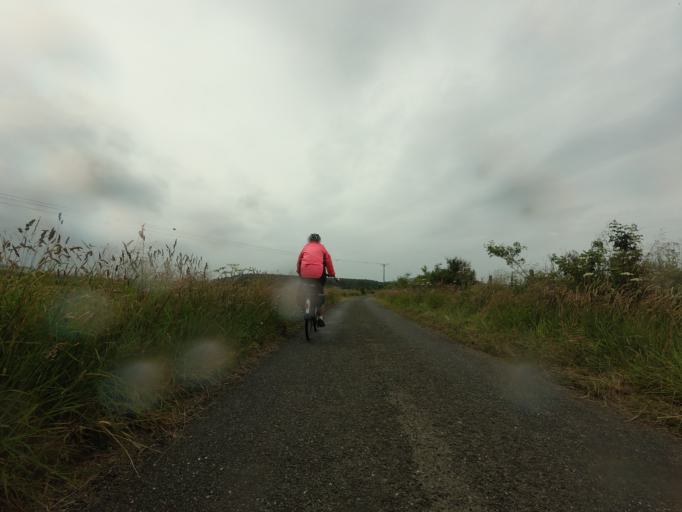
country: GB
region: Scotland
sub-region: Moray
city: Cullen
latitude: 57.6737
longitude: -2.7929
